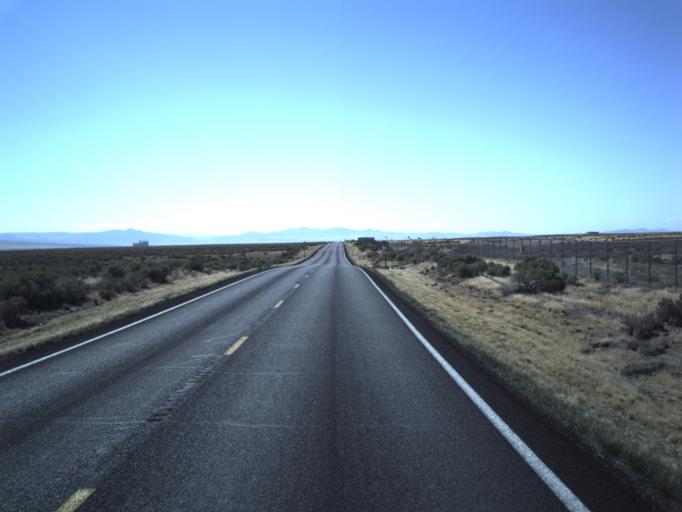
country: US
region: Utah
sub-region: Beaver County
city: Milford
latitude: 38.4327
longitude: -113.0098
